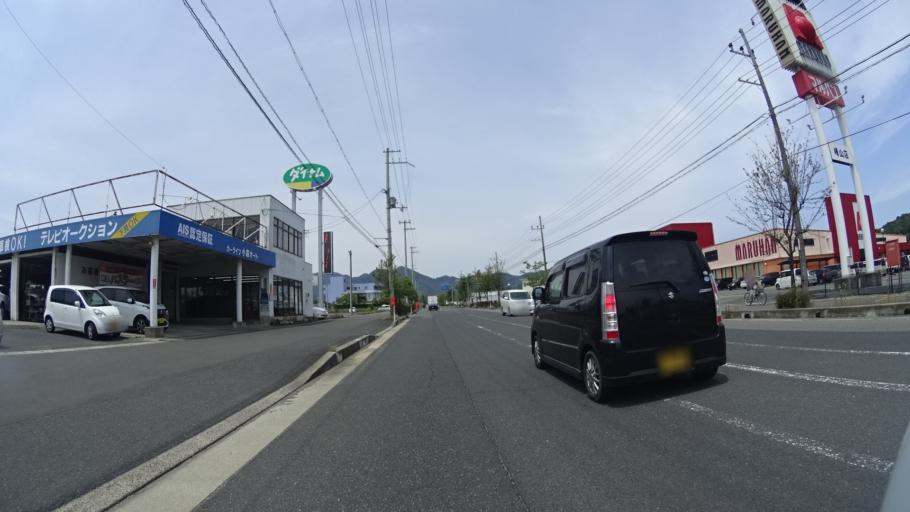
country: JP
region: Kyoto
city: Miyazu
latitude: 35.6093
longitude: 135.0690
